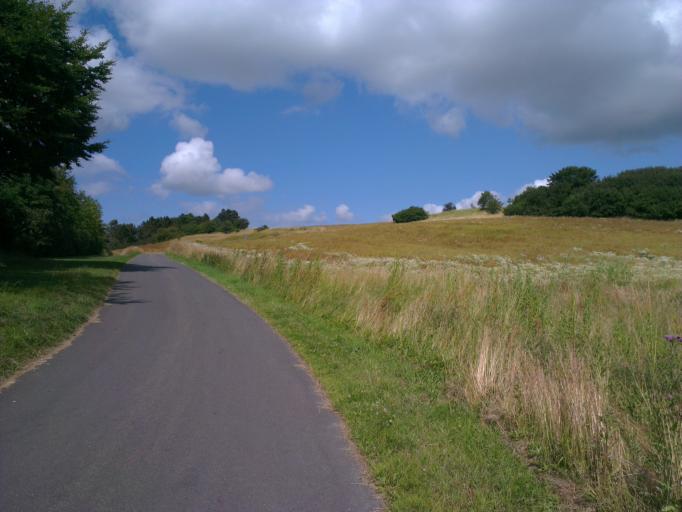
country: DK
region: Zealand
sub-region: Lejre Kommune
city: Ejby
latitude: 55.7380
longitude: 11.8673
